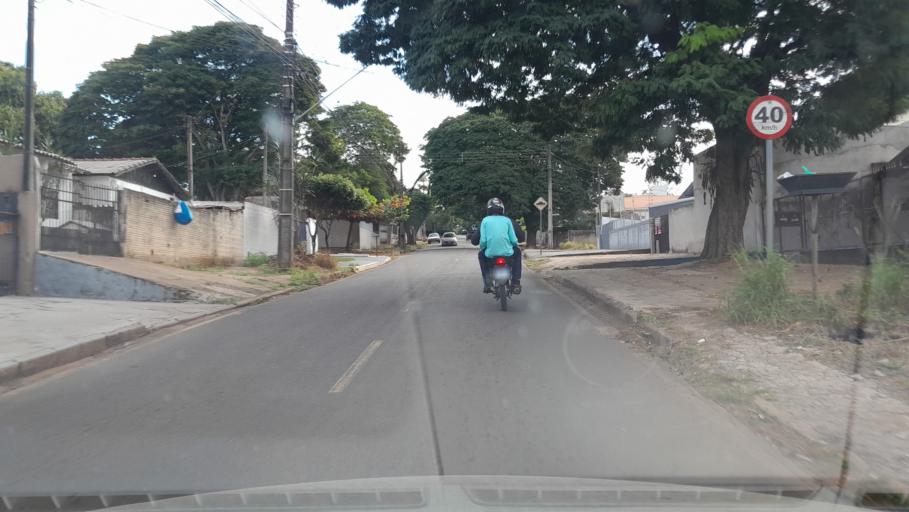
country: BR
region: Parana
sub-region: Umuarama
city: Umuarama
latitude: -23.7720
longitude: -53.3060
